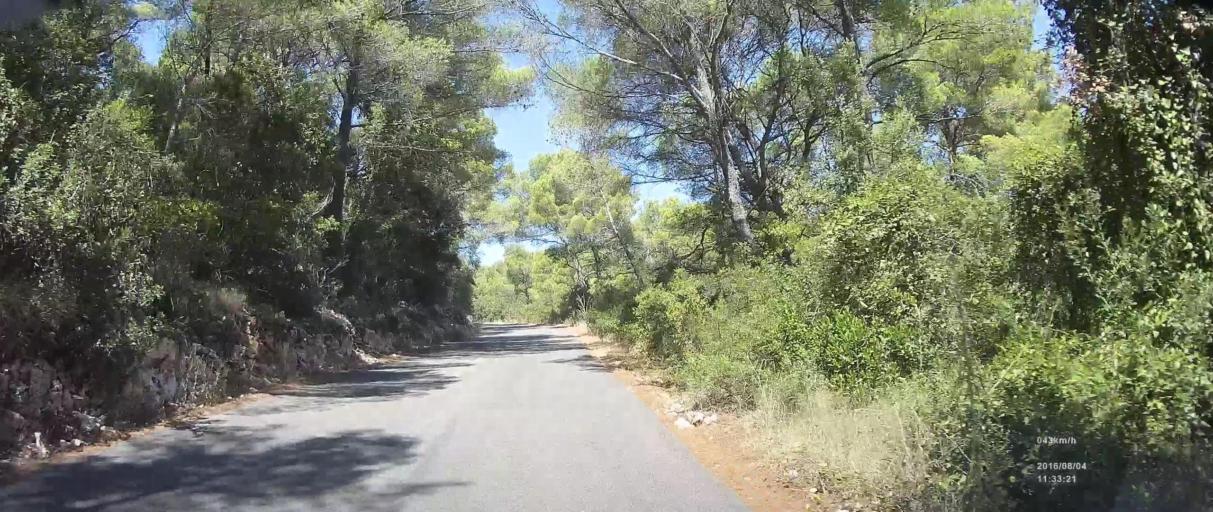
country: HR
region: Dubrovacko-Neretvanska
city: Blato
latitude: 42.7884
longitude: 17.3692
